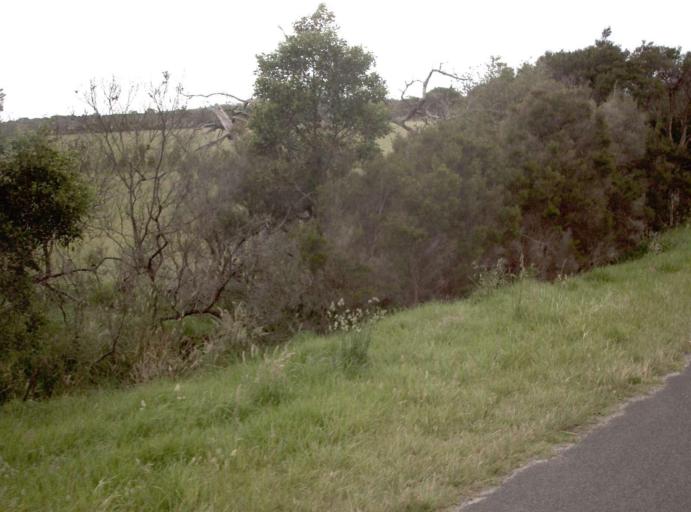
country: AU
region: Victoria
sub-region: Cardinia
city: Koo-Wee-Rup
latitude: -38.3071
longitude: 145.5731
